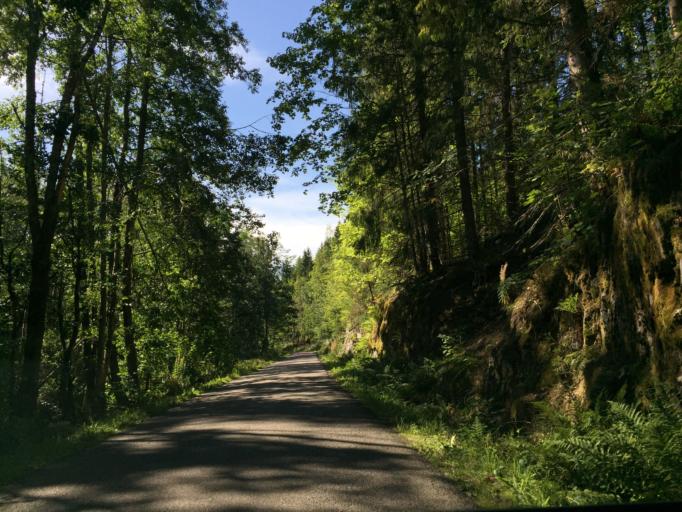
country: NO
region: Vestfold
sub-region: Hof
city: Hof
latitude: 59.4795
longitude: 10.1492
